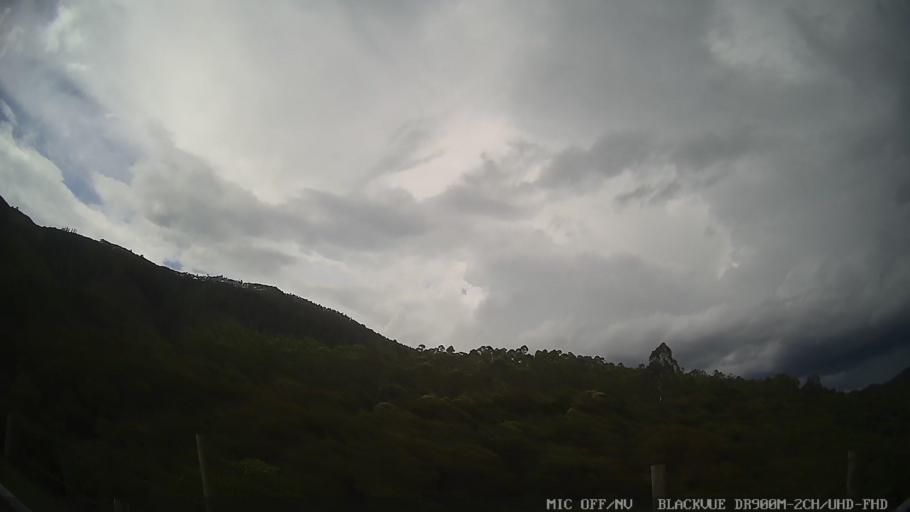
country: BR
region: Sao Paulo
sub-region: Santa Branca
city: Santa Branca
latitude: -23.5253
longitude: -45.7586
